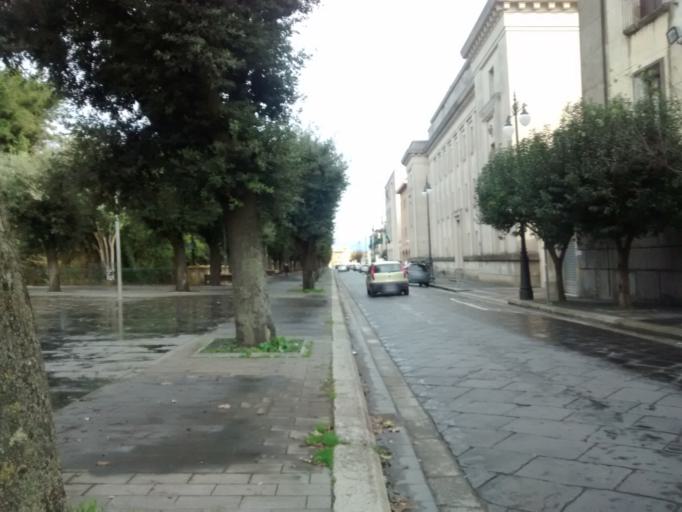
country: IT
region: Calabria
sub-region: Provincia di Vibo-Valentia
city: Vibo Valentia
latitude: 38.6744
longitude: 16.1057
